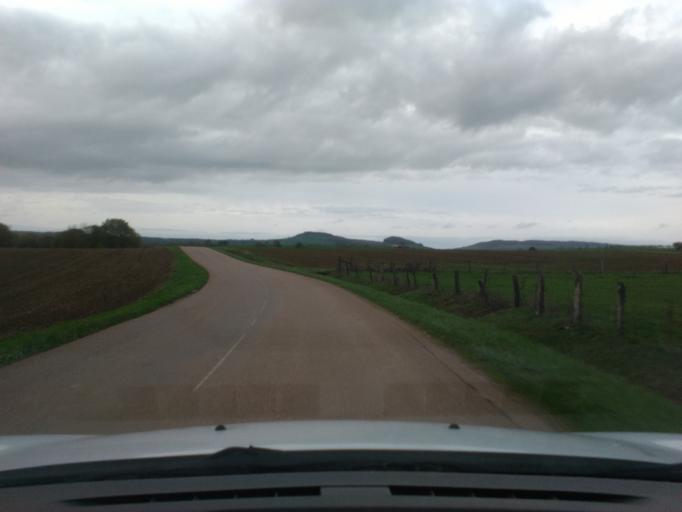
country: FR
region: Lorraine
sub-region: Departement des Vosges
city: Mirecourt
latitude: 48.3442
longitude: 6.1042
